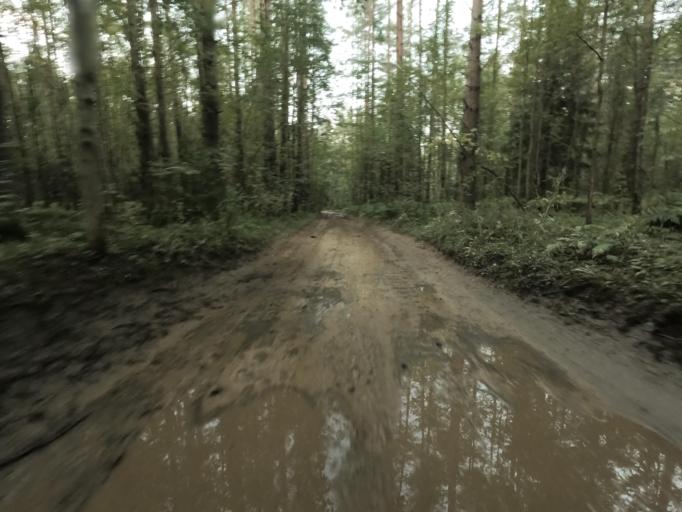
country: RU
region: Leningrad
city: Otradnoye
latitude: 59.8506
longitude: 30.7961
